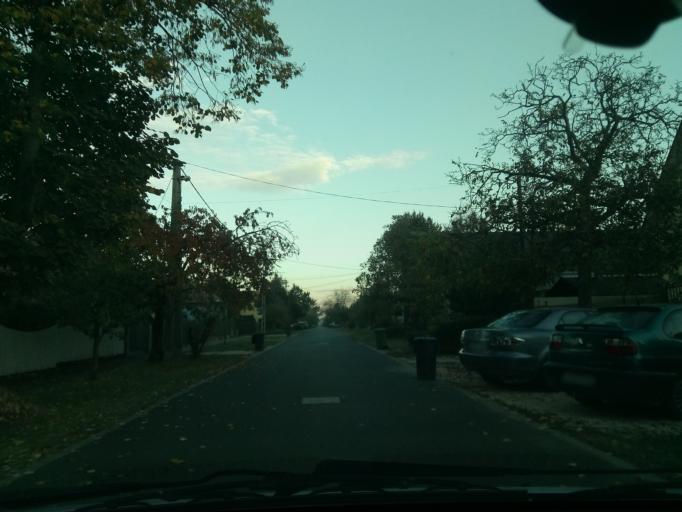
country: HU
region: Pest
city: Gyal
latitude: 47.4291
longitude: 19.2275
